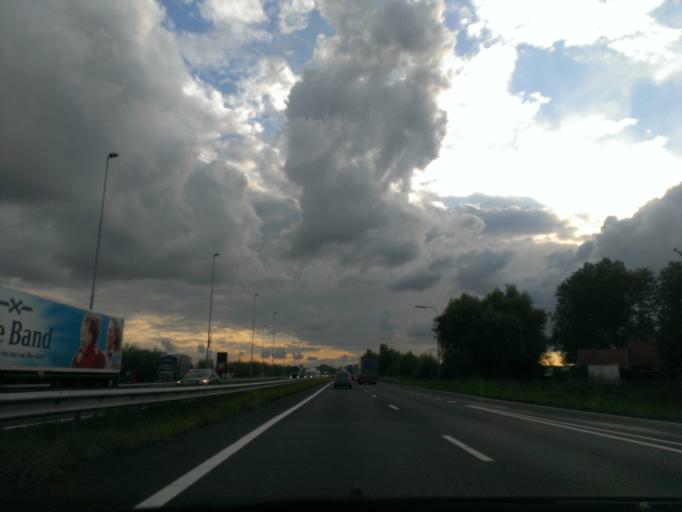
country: NL
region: South Holland
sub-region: Gemeente Hardinxveld-Giessendam
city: Boven-Hardinxveld
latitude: 51.8311
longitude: 4.8797
